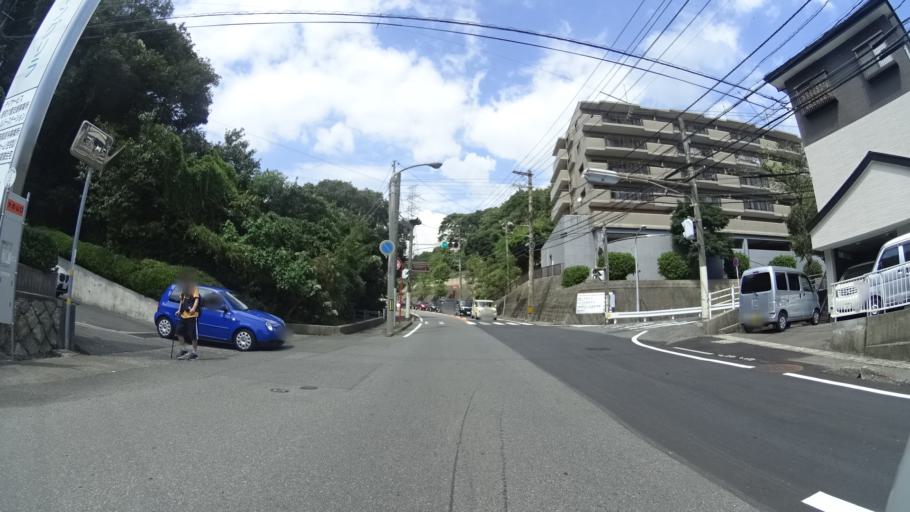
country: JP
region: Yamaguchi
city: Shimonoseki
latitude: 33.9683
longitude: 130.9545
